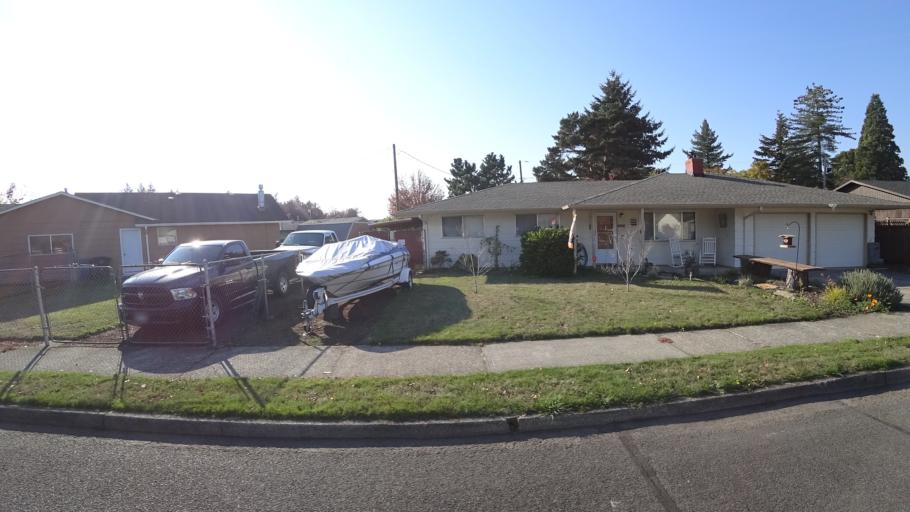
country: US
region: Oregon
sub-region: Multnomah County
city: Gresham
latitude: 45.5141
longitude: -122.4325
